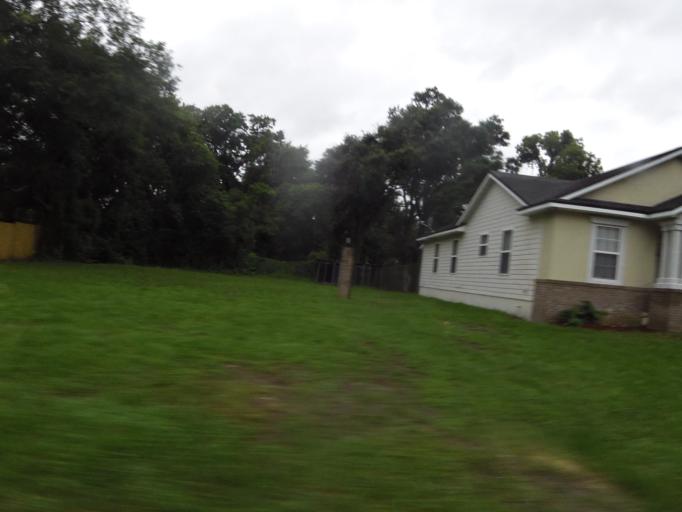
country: US
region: Florida
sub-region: Duval County
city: Jacksonville
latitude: 30.3593
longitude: -81.6392
